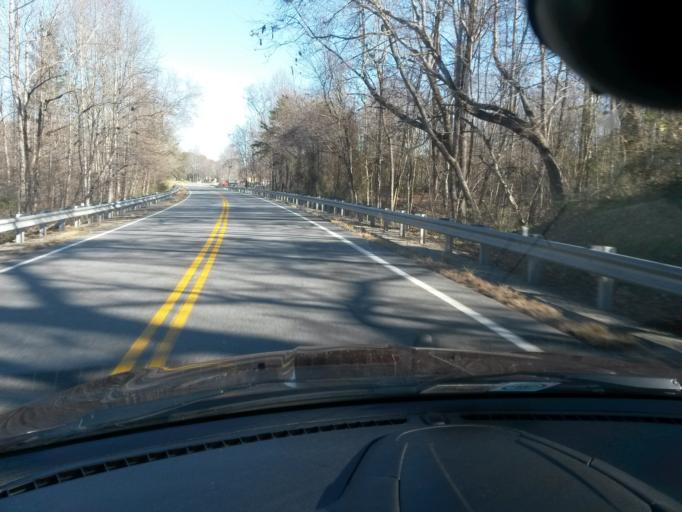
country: US
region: Virginia
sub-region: Henry County
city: Pannill Fork
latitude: 36.7779
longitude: -80.1346
